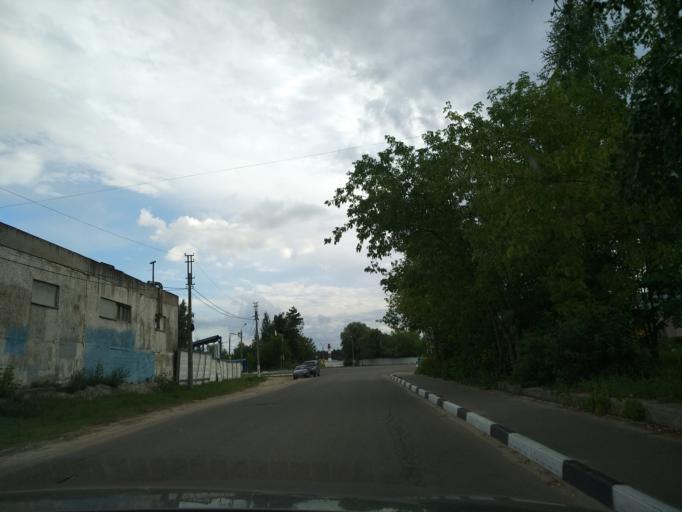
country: RU
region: Moskovskaya
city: Yegor'yevsk
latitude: 55.3656
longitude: 39.0786
